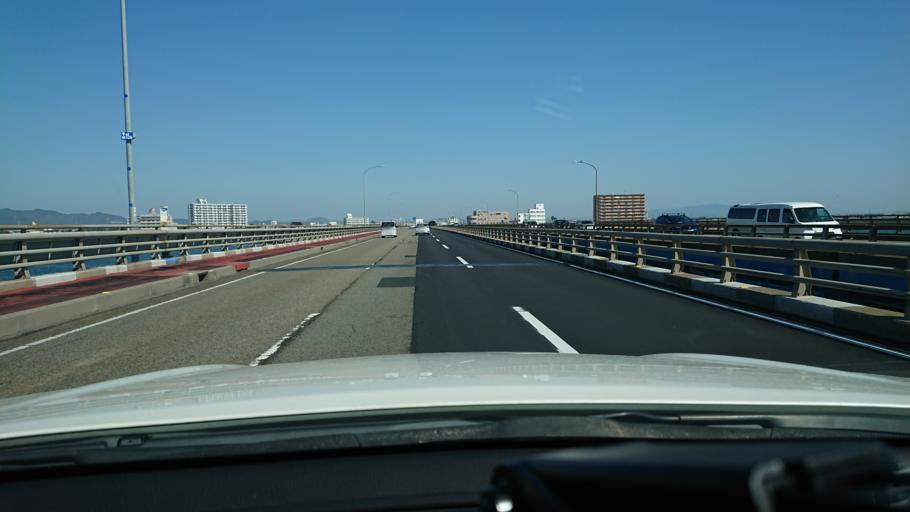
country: JP
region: Tokushima
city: Tokushima-shi
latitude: 34.0907
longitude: 134.5687
